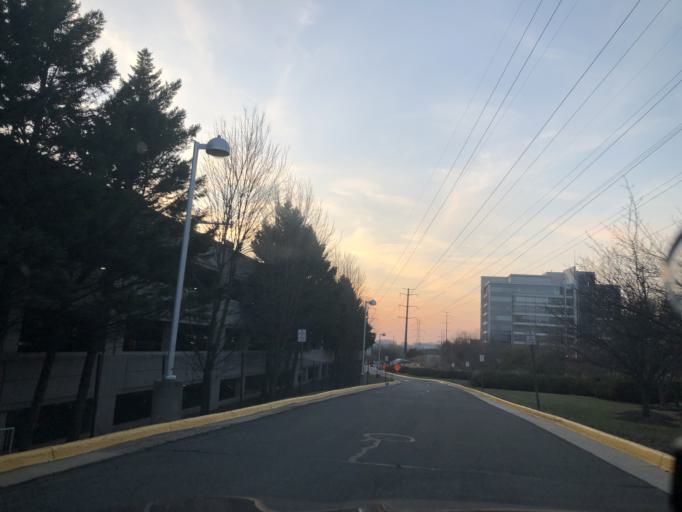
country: US
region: Virginia
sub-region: Fairfax County
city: Reston
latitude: 38.9563
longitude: -77.3590
